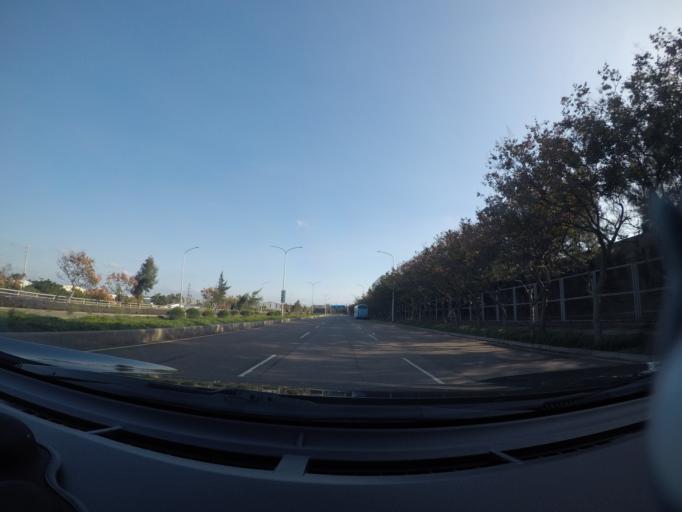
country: TW
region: Taiwan
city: Taoyuan City
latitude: 25.0976
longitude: 121.2560
